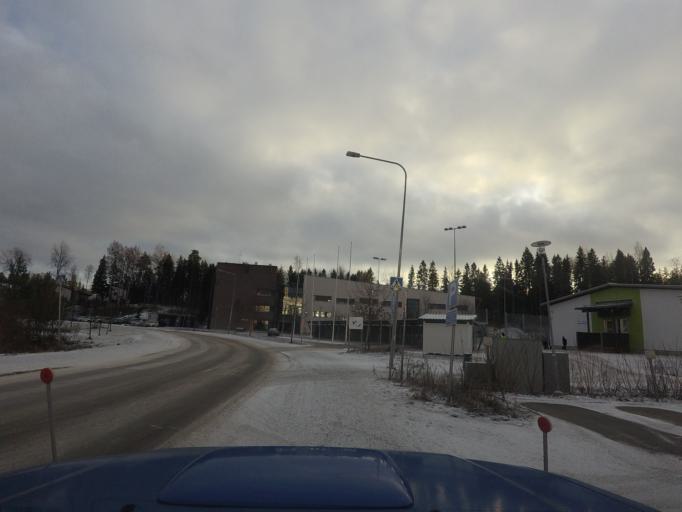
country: FI
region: Uusimaa
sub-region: Helsinki
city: Kauniainen
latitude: 60.2057
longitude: 24.7103
